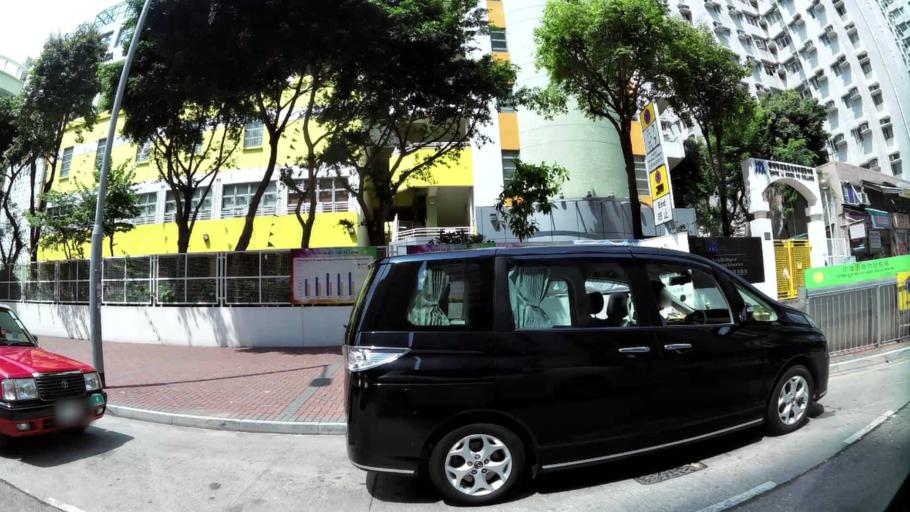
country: HK
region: Sham Shui Po
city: Sham Shui Po
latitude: 22.3141
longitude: 114.1642
